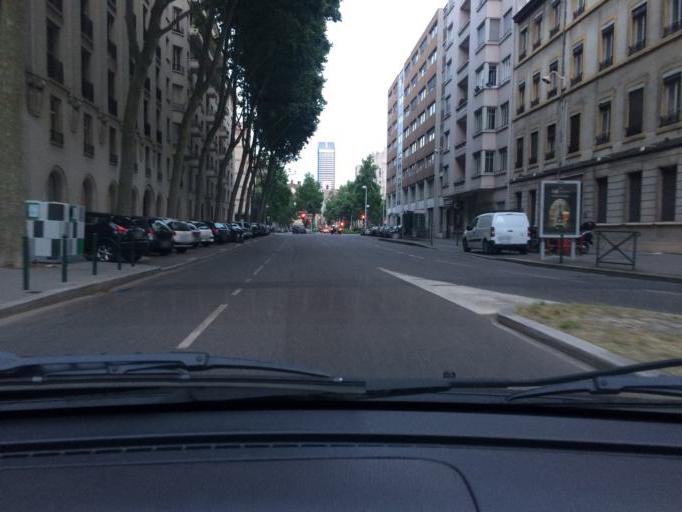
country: FR
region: Rhone-Alpes
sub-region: Departement du Rhone
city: Caluire-et-Cuire
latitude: 45.7731
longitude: 4.8498
